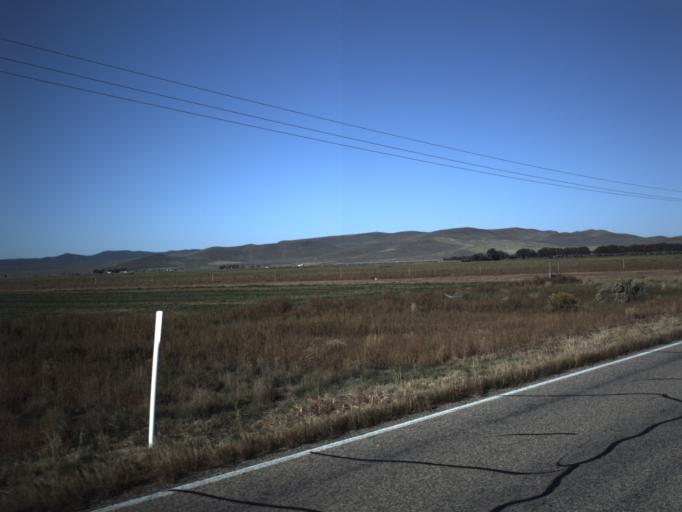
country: US
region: Utah
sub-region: Washington County
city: Enterprise
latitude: 37.7155
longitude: -113.6729
